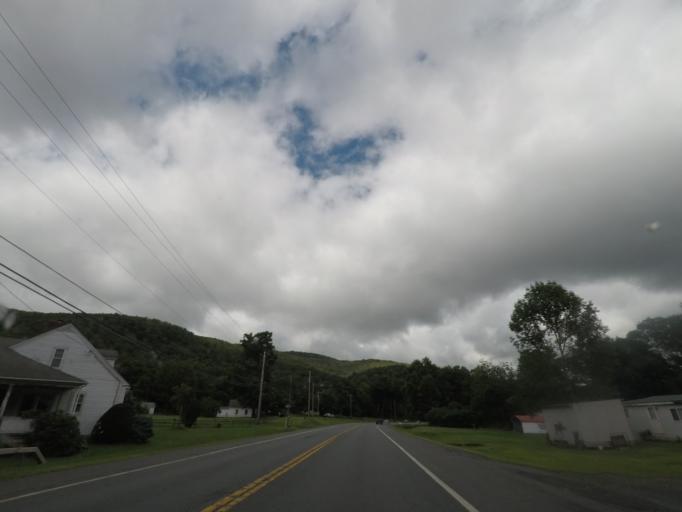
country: US
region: Massachusetts
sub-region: Berkshire County
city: Williamstown
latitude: 42.6606
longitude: -73.3685
